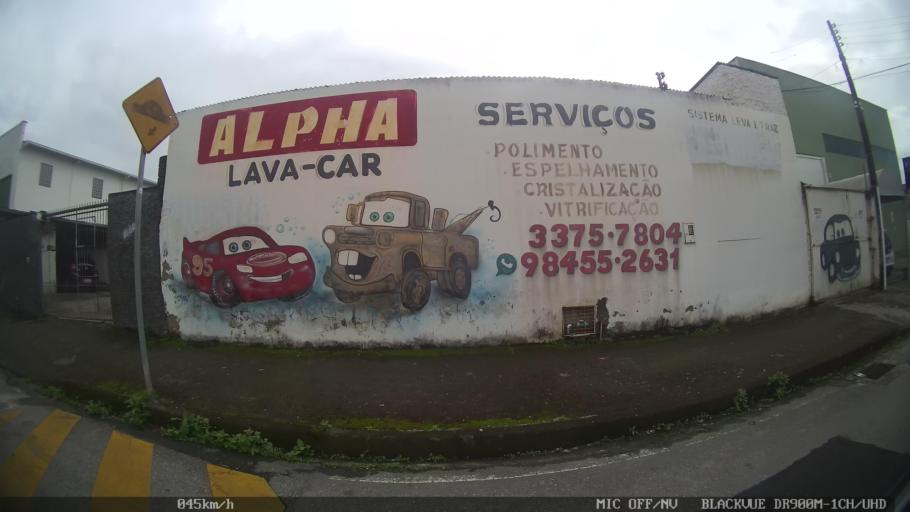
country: BR
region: Santa Catarina
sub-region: Sao Jose
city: Campinas
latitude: -27.5672
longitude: -48.6229
